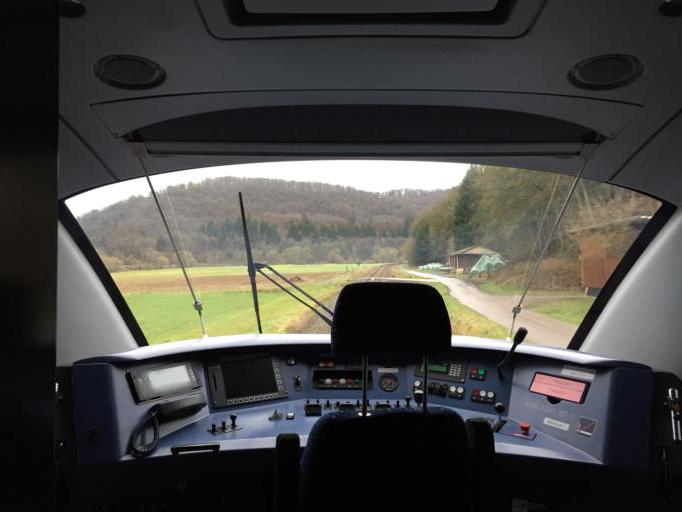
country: DE
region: Hesse
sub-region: Regierungsbezirk Kassel
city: Frankenau
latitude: 51.1210
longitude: 8.8721
